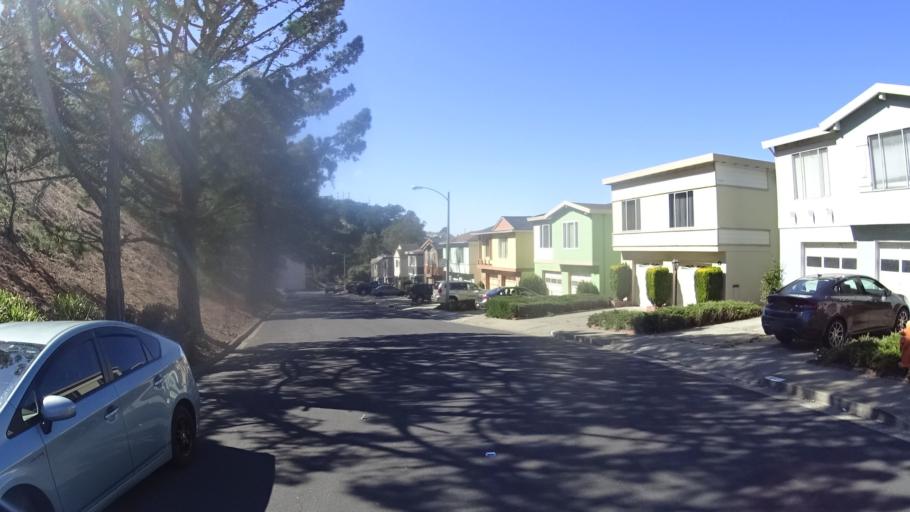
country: US
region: California
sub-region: San Mateo County
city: Daly City
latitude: 37.7057
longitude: -122.4312
